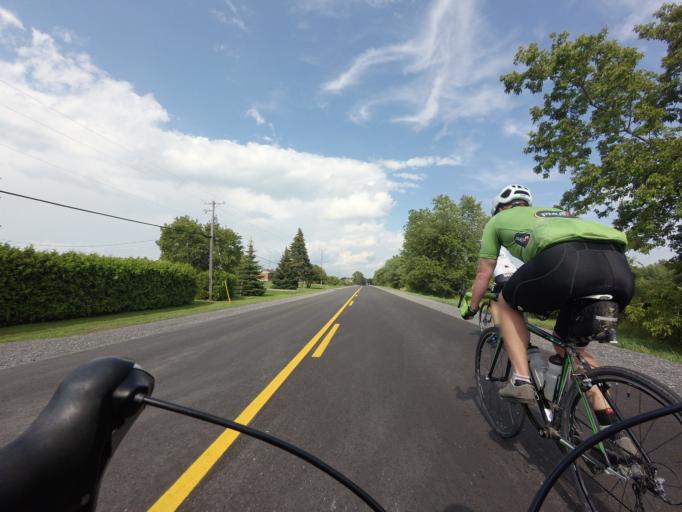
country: CA
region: Ontario
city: Brockville
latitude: 44.7566
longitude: -75.7451
